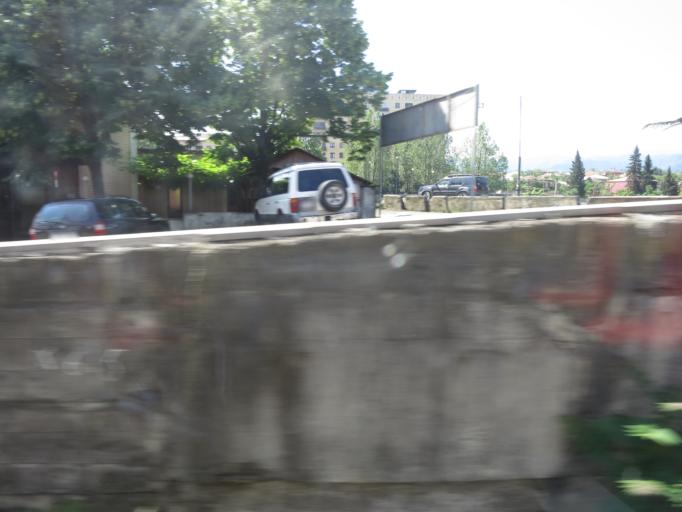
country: GE
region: Imereti
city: Zestap'oni
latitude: 42.1086
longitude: 43.0442
